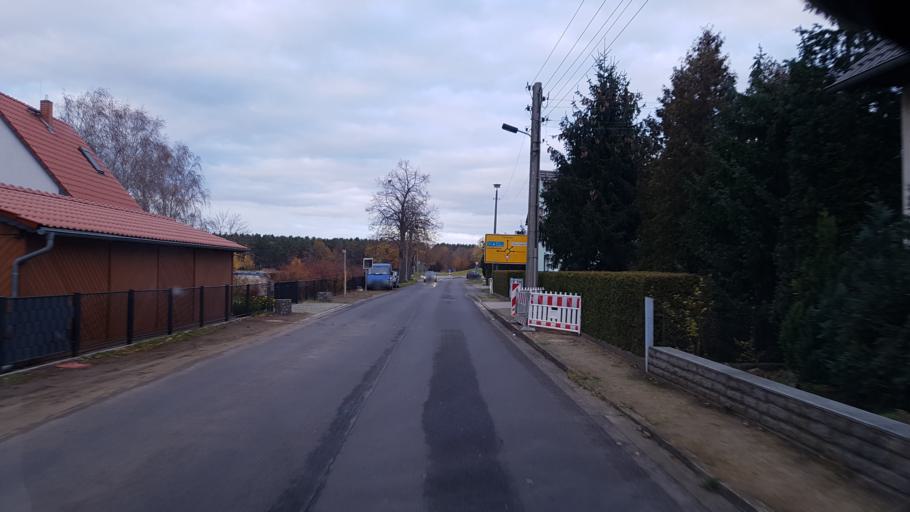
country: DE
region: Brandenburg
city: Ortrand
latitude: 51.3818
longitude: 13.7594
